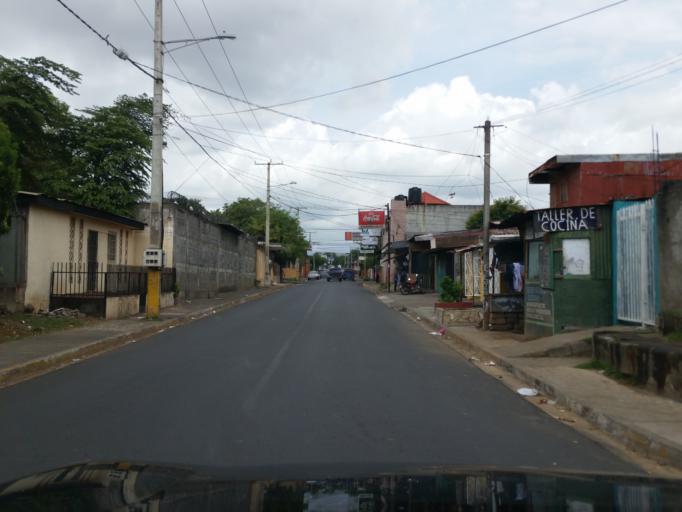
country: NI
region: Managua
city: Managua
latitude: 12.1417
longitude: -86.2530
